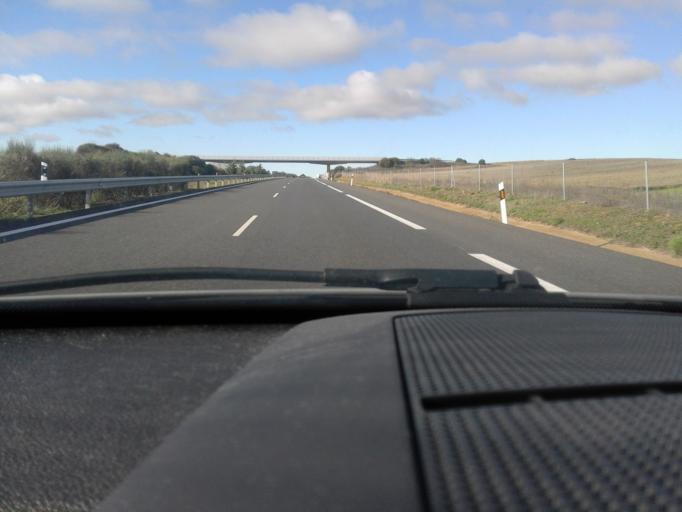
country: ES
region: Castille and Leon
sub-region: Provincia de Palencia
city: Moratinos
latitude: 42.3634
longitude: -4.9222
